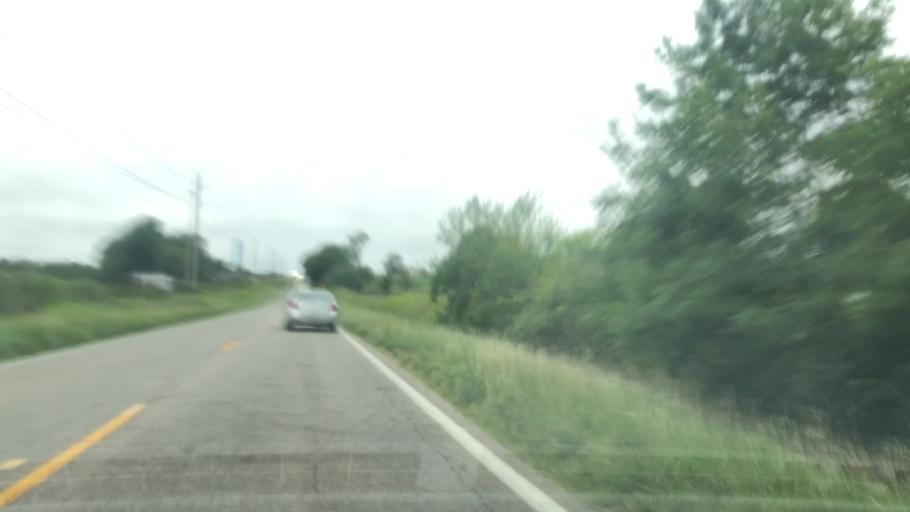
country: US
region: Oklahoma
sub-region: Washington County
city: Dewey
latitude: 36.7280
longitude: -95.8497
